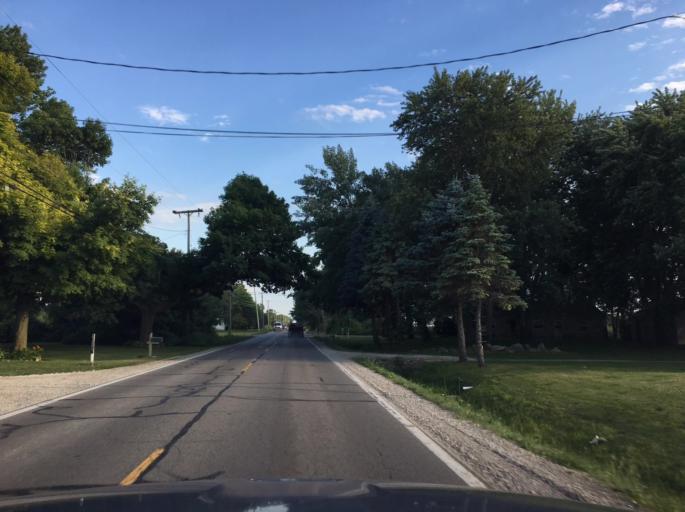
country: US
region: Michigan
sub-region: Macomb County
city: Romeo
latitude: 42.7465
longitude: -82.9606
